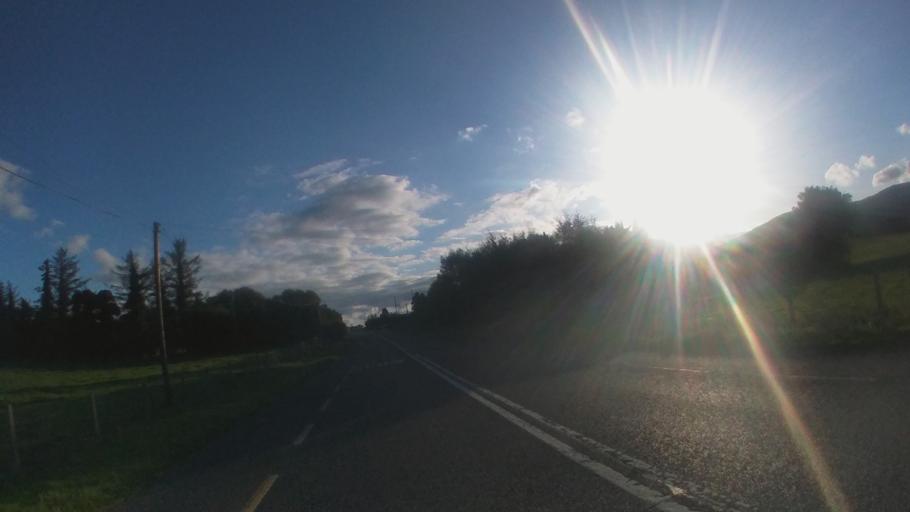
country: IE
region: Leinster
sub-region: Lu
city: Carlingford
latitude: 54.0118
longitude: -6.1644
